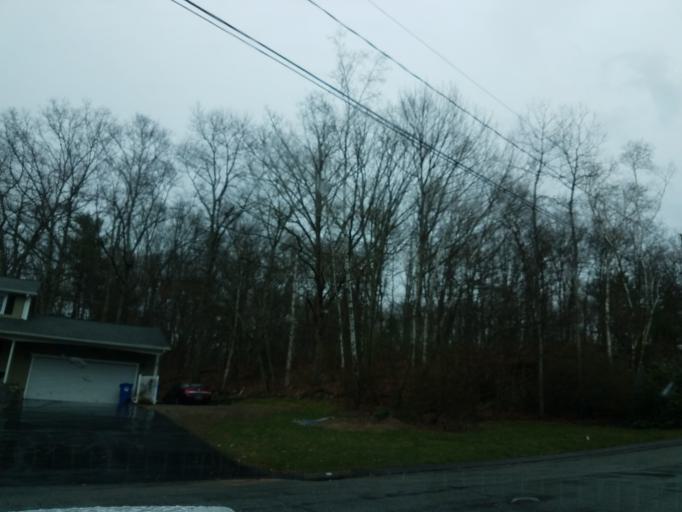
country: US
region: Connecticut
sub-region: Tolland County
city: Tolland
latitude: 41.8664
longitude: -72.4070
